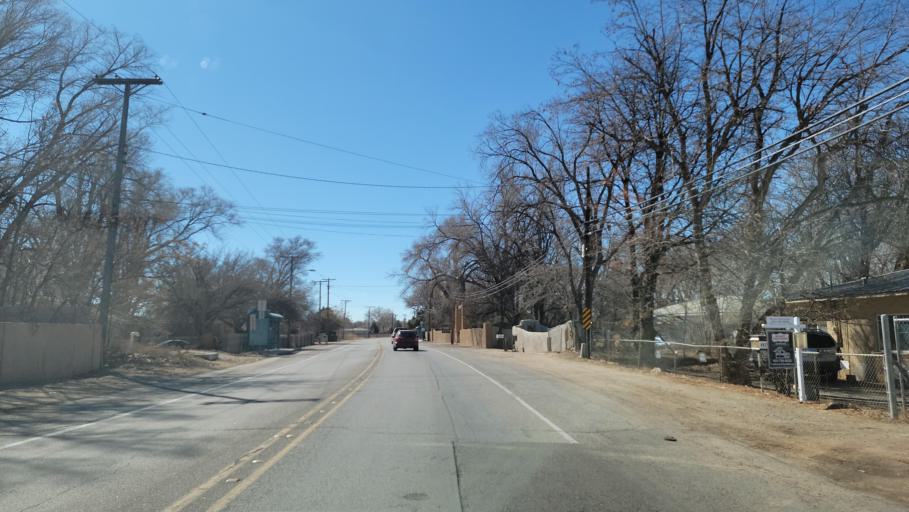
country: US
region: New Mexico
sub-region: Bernalillo County
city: South Valley
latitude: 35.0018
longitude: -106.6912
